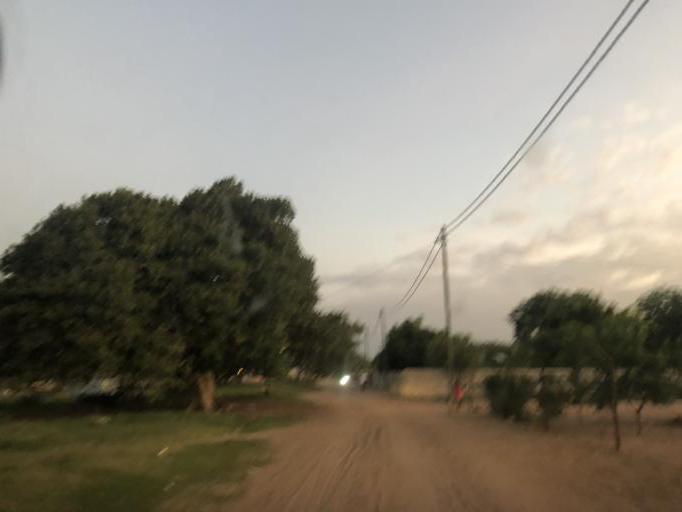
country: AO
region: Cunene
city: Ondjiva
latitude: -17.0632
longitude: 15.7073
